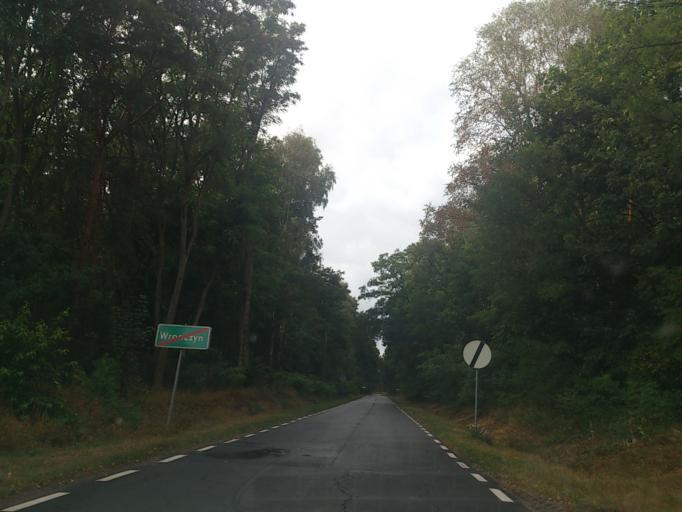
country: PL
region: Greater Poland Voivodeship
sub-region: Powiat poznanski
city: Pobiedziska
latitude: 52.5080
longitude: 17.2059
